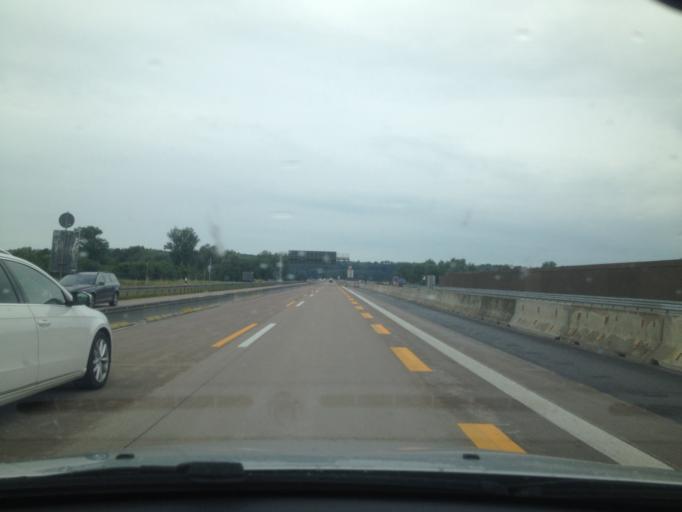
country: DE
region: Bavaria
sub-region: Swabia
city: Rofingen
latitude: 48.4126
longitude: 10.4277
